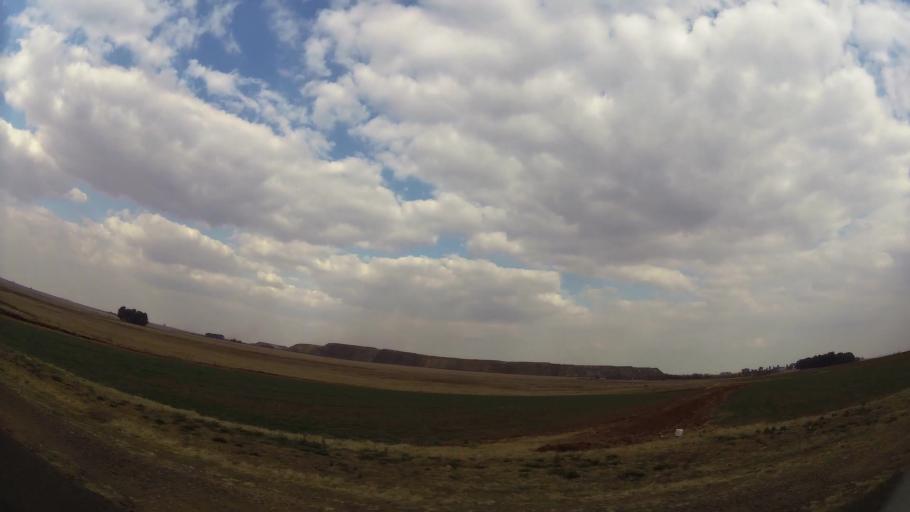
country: ZA
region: Mpumalanga
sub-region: Nkangala District Municipality
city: Delmas
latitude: -26.2148
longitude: 28.6760
